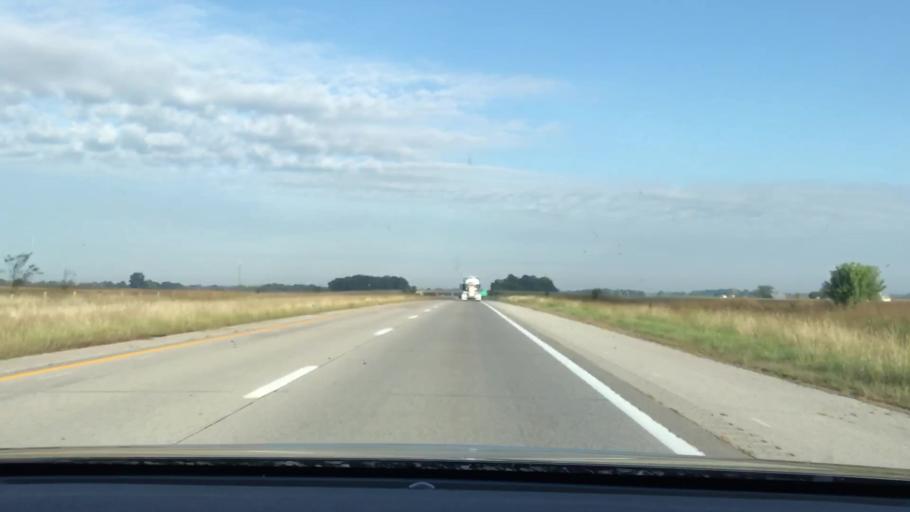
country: US
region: Kentucky
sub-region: Christian County
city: Hopkinsville
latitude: 36.8011
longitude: -87.6104
